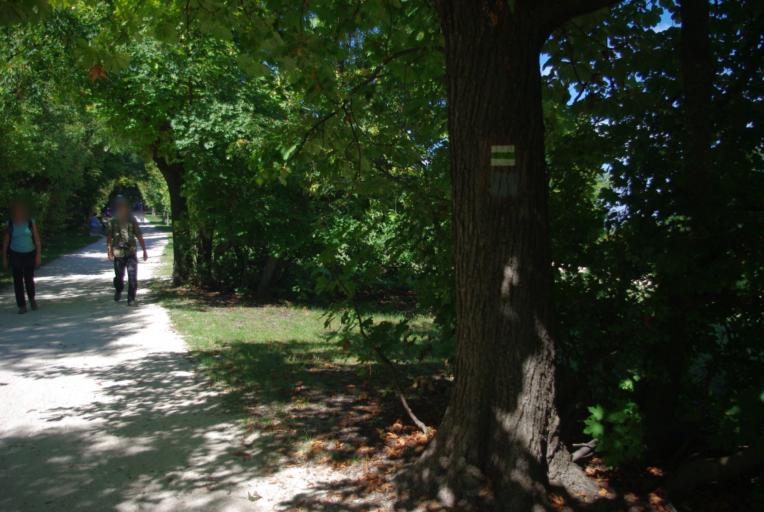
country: HU
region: Pest
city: Budaors
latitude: 47.5019
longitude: 18.9685
